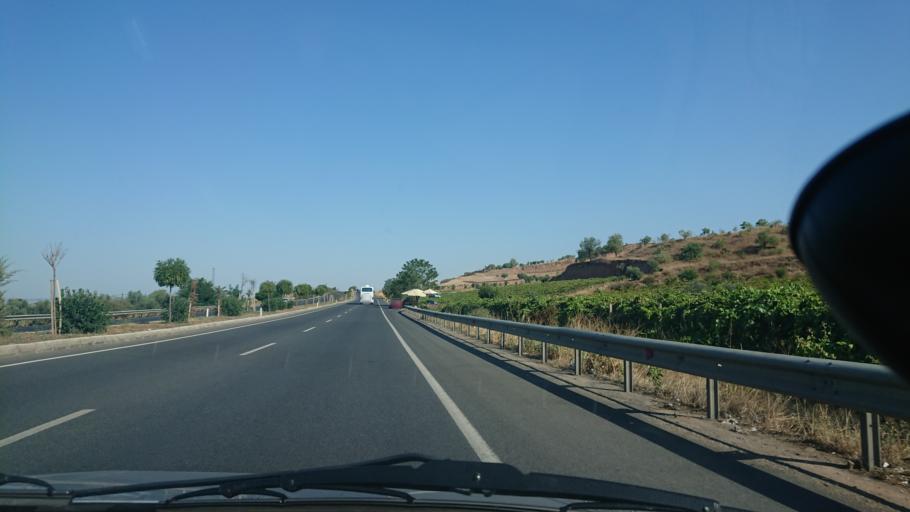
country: TR
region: Manisa
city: Ahmetli
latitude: 38.5107
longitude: 27.9720
